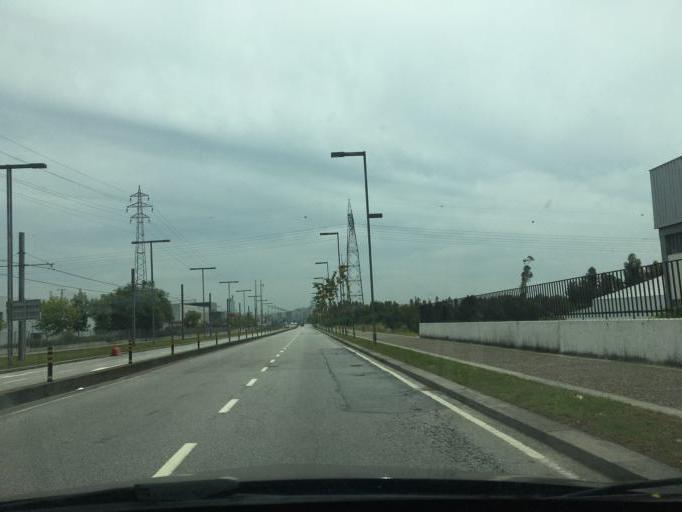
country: PT
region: Porto
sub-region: Maia
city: Maia
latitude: 41.2484
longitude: -8.6304
